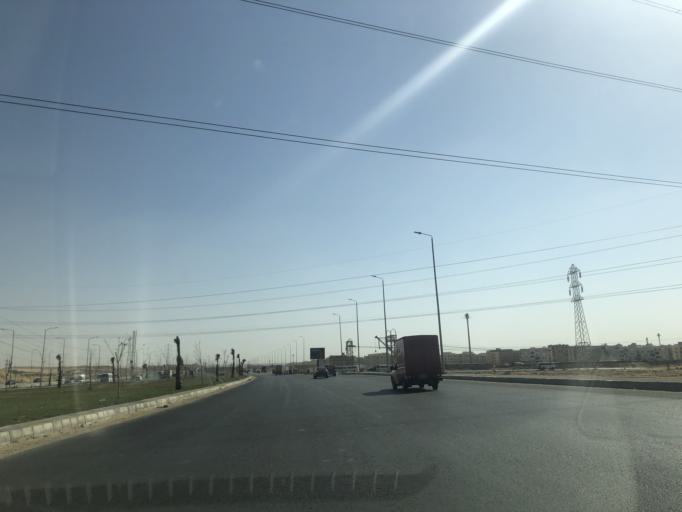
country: EG
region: Al Jizah
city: Madinat Sittah Uktubar
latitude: 29.9467
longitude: 30.9495
